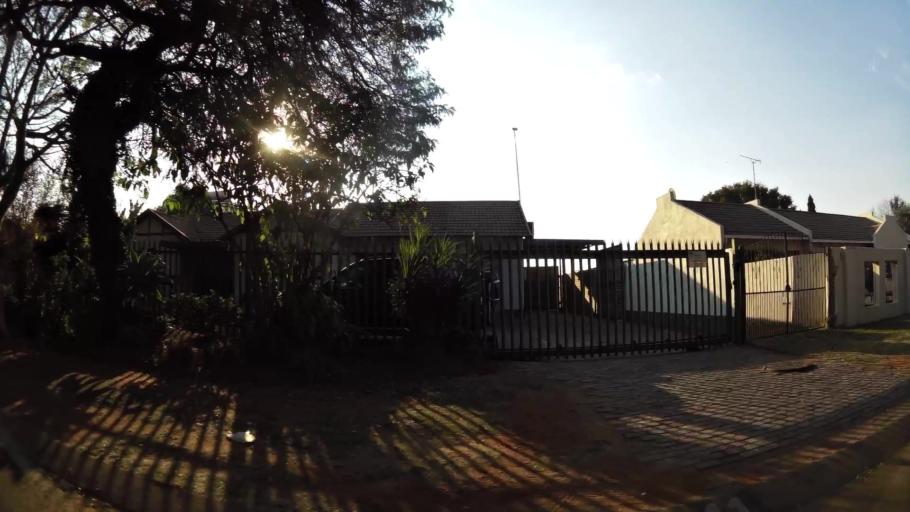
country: ZA
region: Gauteng
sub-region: City of Johannesburg Metropolitan Municipality
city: Modderfontein
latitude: -26.0706
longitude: 28.2108
